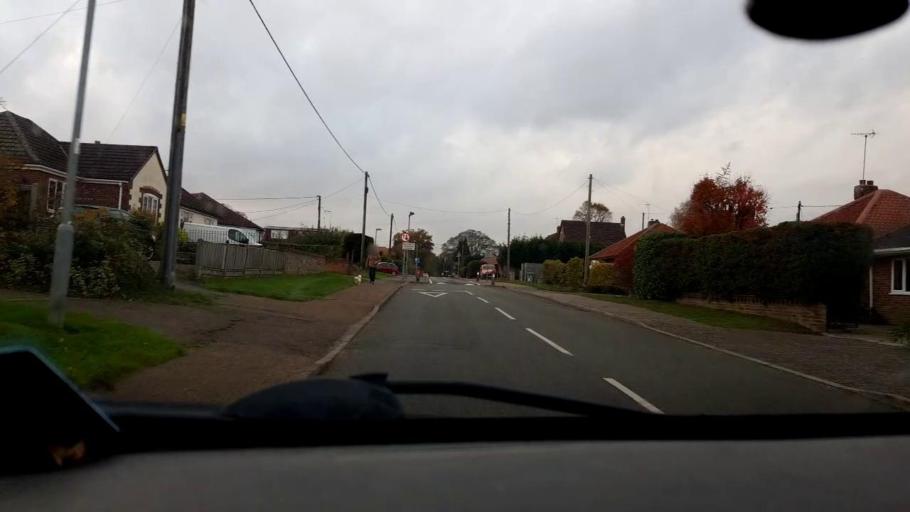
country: GB
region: England
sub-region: Norfolk
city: Spixworth
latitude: 52.6878
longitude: 1.3201
